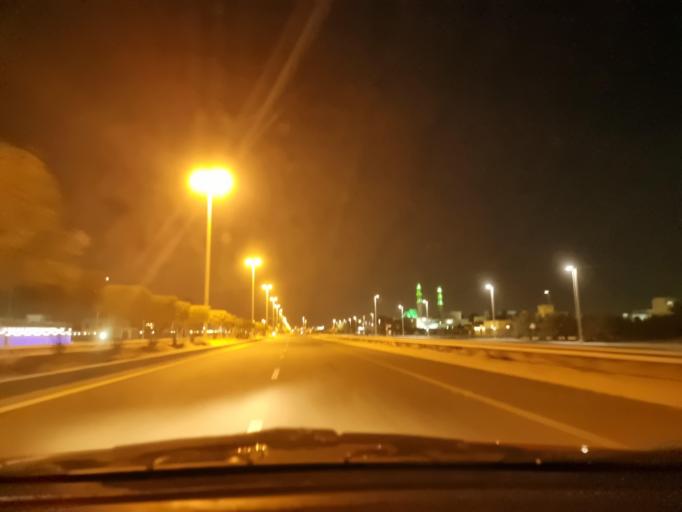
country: AE
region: Abu Dhabi
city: Abu Dhabi
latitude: 24.3715
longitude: 54.7014
